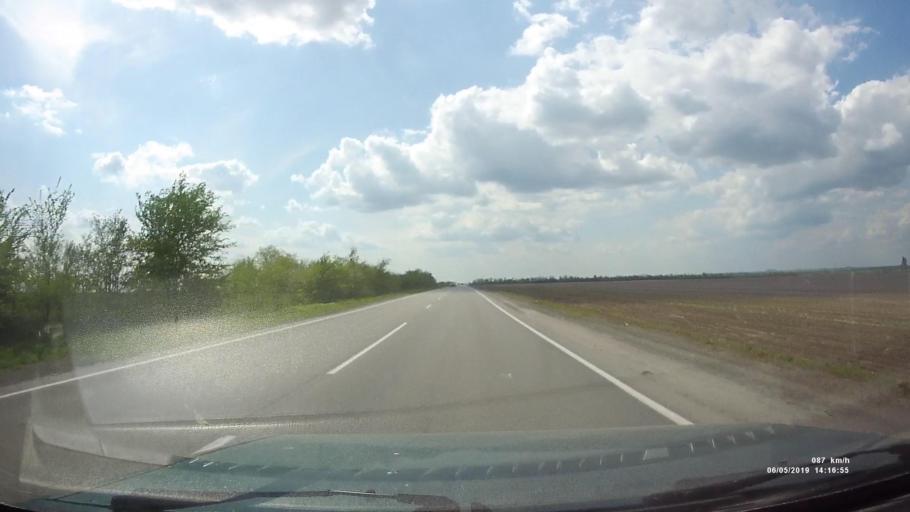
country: RU
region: Rostov
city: Kamenolomni
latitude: 47.6344
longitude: 40.2782
